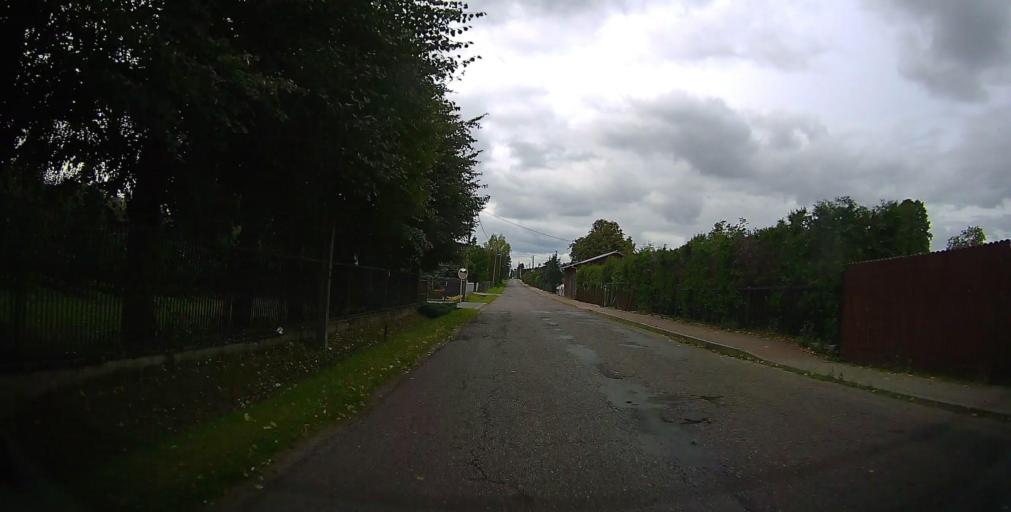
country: PL
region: Masovian Voivodeship
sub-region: Powiat grojecki
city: Belsk Duzy
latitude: 51.8217
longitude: 20.8180
